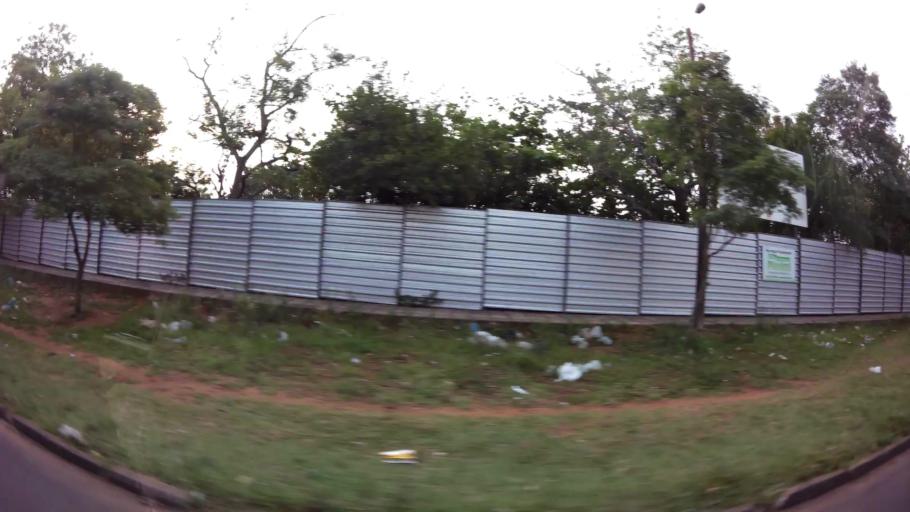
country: PY
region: Central
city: Lambare
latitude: -25.3209
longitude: -57.5780
